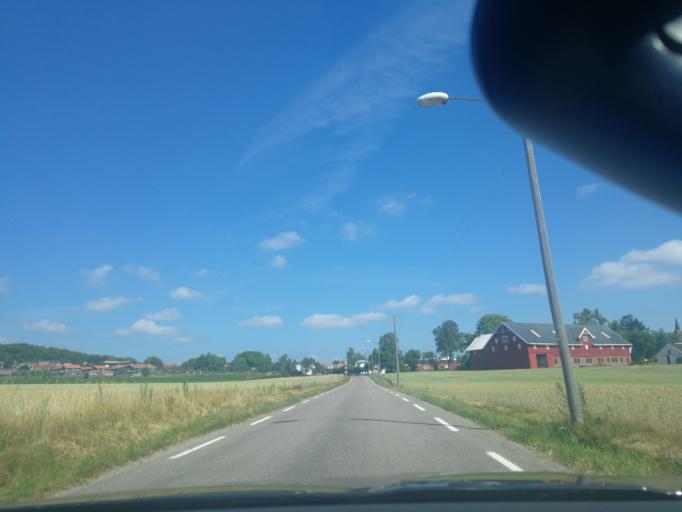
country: NO
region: Vestfold
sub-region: Stokke
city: Stokke
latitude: 59.2158
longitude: 10.2965
